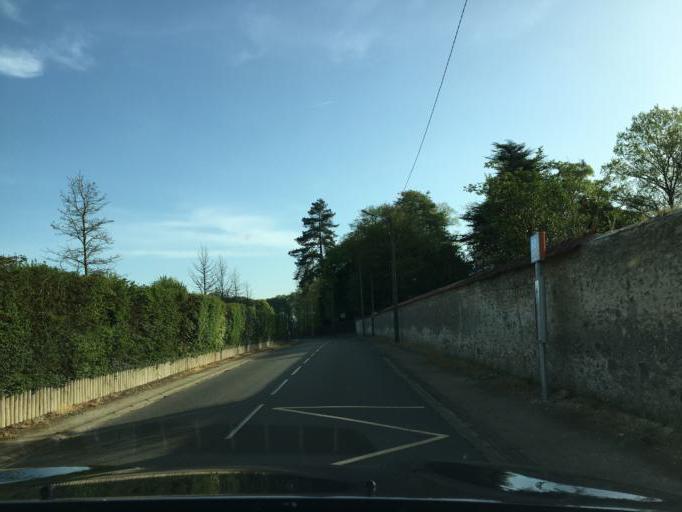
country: FR
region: Ile-de-France
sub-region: Departement des Yvelines
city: Conde-sur-Vesgre
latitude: 48.6806
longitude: 1.6527
